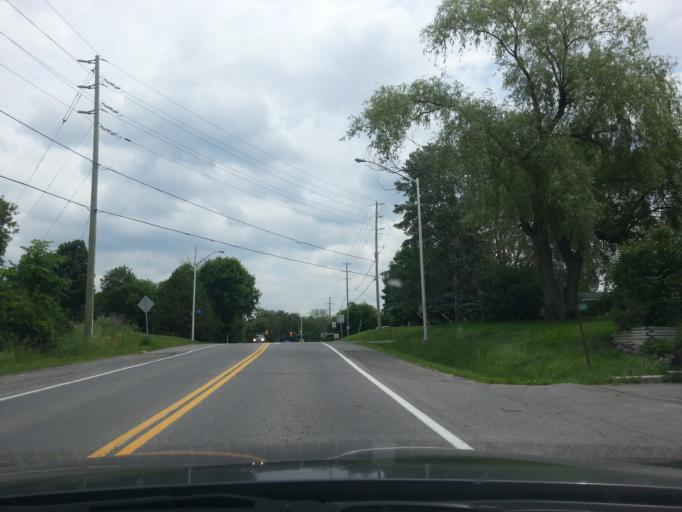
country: CA
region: Ontario
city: Bells Corners
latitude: 45.2278
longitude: -75.6915
